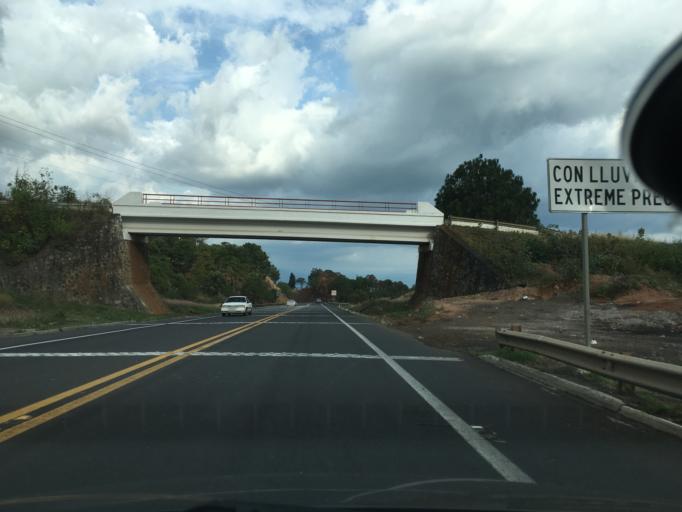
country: MX
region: Michoacan
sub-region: Uruapan
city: Toreo Bajo (El Toreo Bajo)
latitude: 19.4185
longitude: -101.9843
